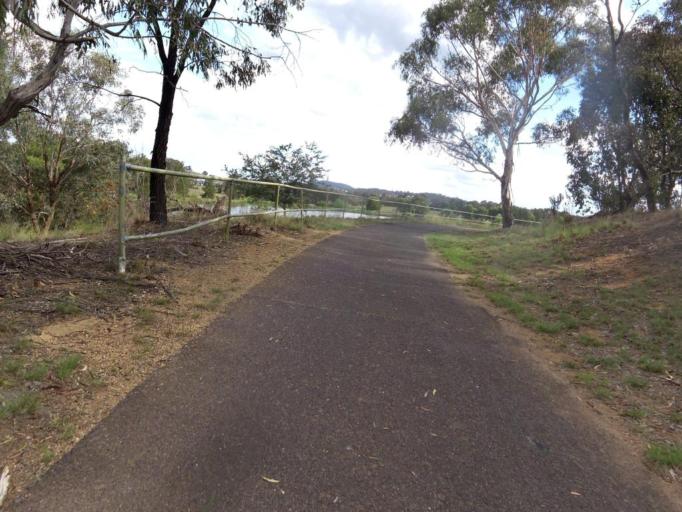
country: AU
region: Australian Capital Territory
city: Belconnen
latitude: -35.2228
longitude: 149.0810
